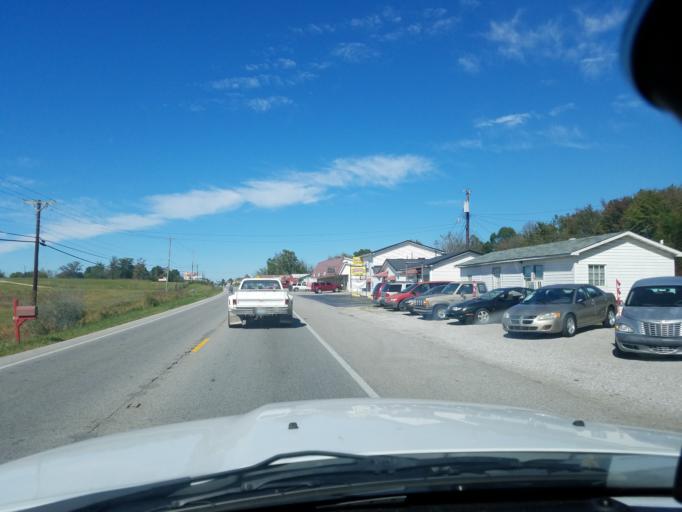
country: US
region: Kentucky
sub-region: Laurel County
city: London
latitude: 37.0831
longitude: -84.0603
